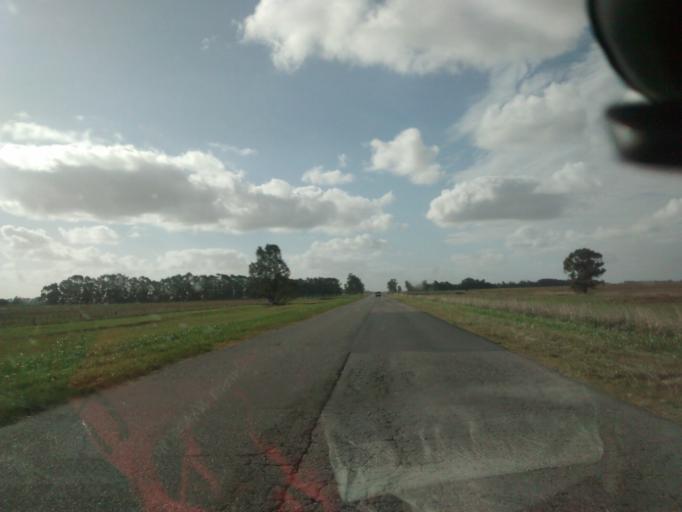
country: AR
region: Buenos Aires
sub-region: Partido de Ayacucho
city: Ayacucho
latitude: -37.2223
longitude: -58.4976
